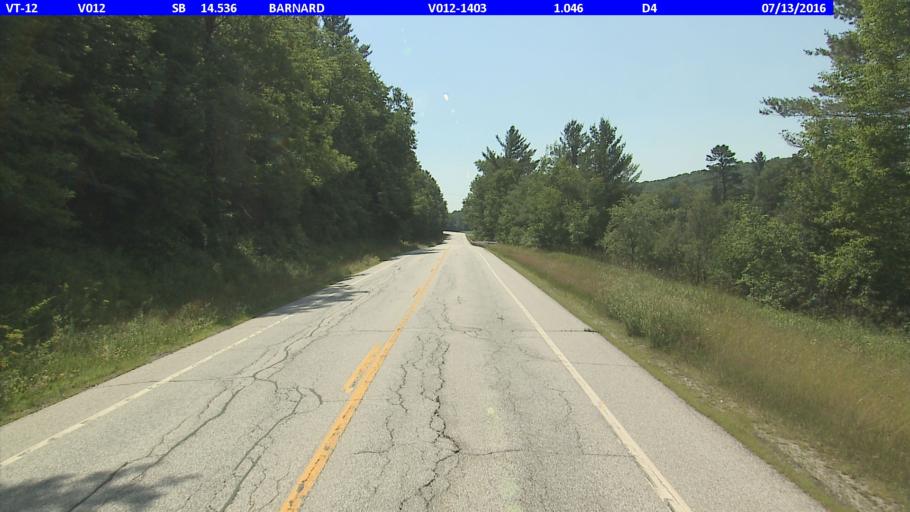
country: US
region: Vermont
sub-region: Windsor County
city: Woodstock
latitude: 43.6832
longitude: -72.5978
